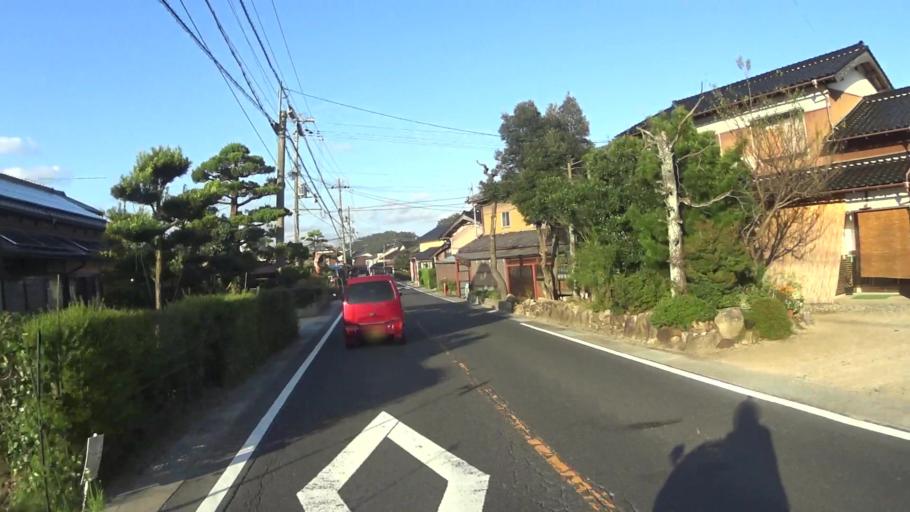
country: JP
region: Kyoto
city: Miyazu
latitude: 35.5906
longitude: 135.0394
